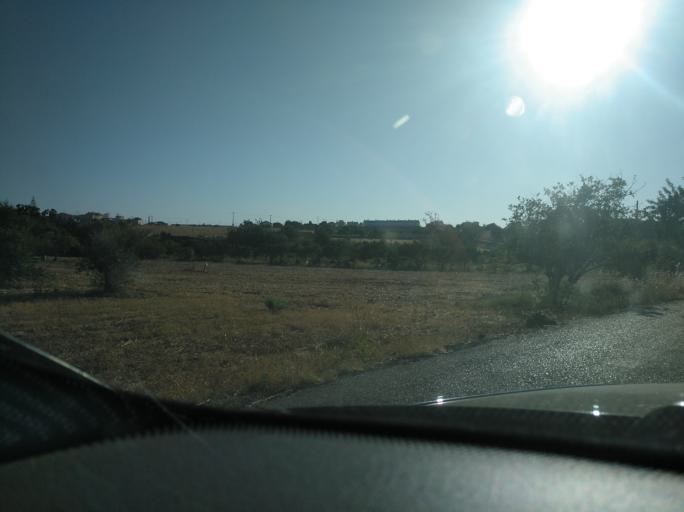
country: PT
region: Faro
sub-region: Vila Real de Santo Antonio
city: Monte Gordo
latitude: 37.1836
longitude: -7.5113
